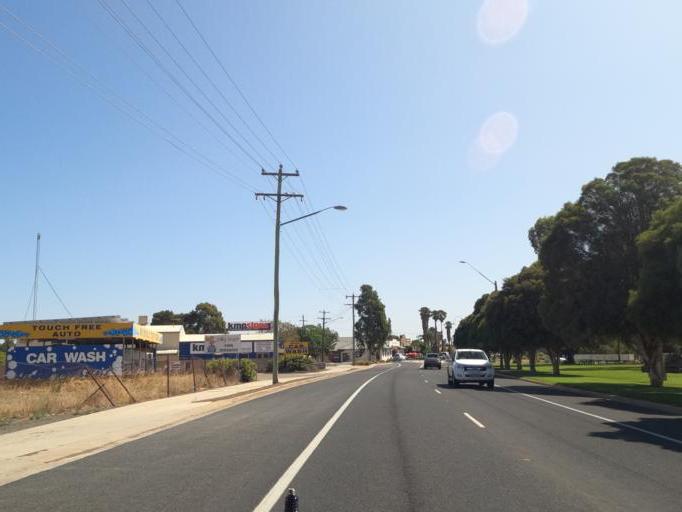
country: AU
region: New South Wales
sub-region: Corowa Shire
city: Mulwala
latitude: -35.9935
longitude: 146.0016
